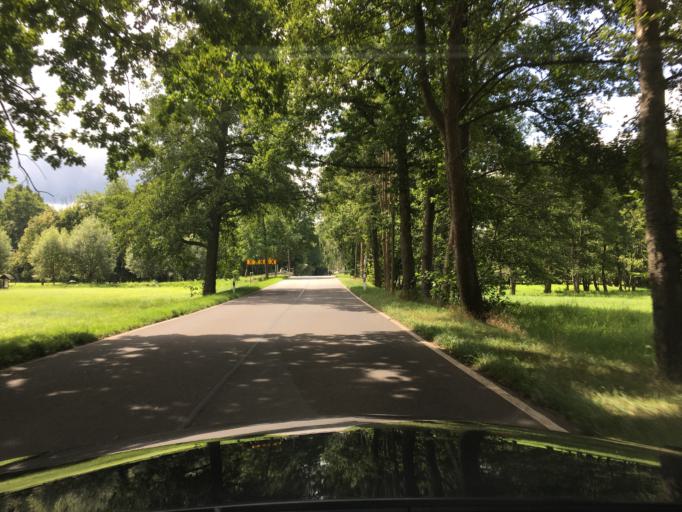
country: DE
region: Brandenburg
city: Burg
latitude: 51.8327
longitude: 14.1050
